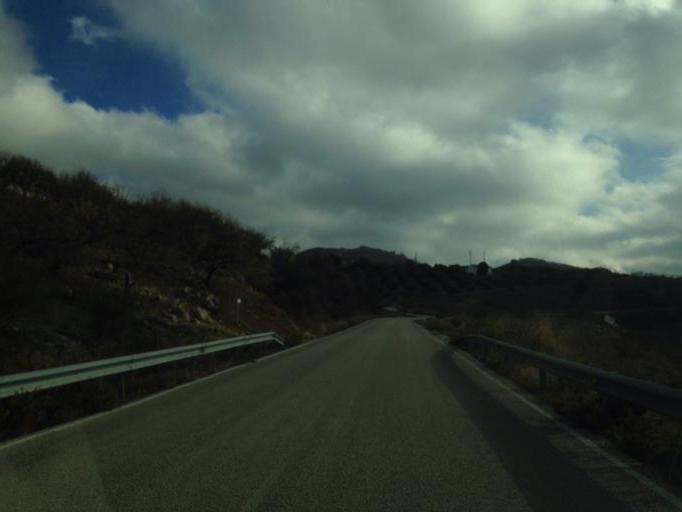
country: ES
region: Andalusia
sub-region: Provincia de Malaga
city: Colmenar
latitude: 36.9327
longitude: -4.3749
